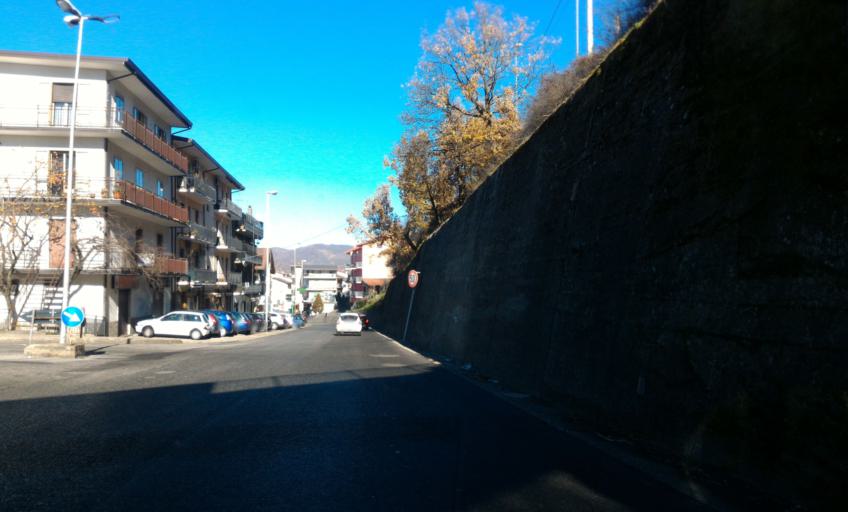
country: IT
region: Calabria
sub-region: Provincia di Cosenza
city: Spezzano della Sila
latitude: 39.3015
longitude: 16.3407
